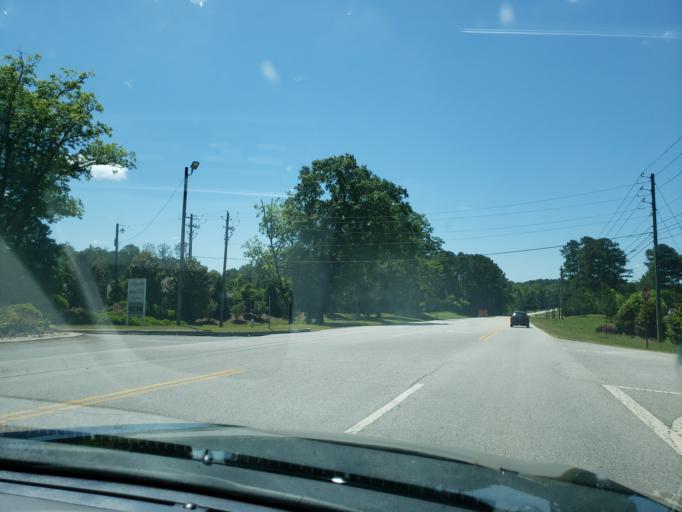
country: US
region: Alabama
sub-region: Lee County
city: Auburn
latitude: 32.6532
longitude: -85.4851
